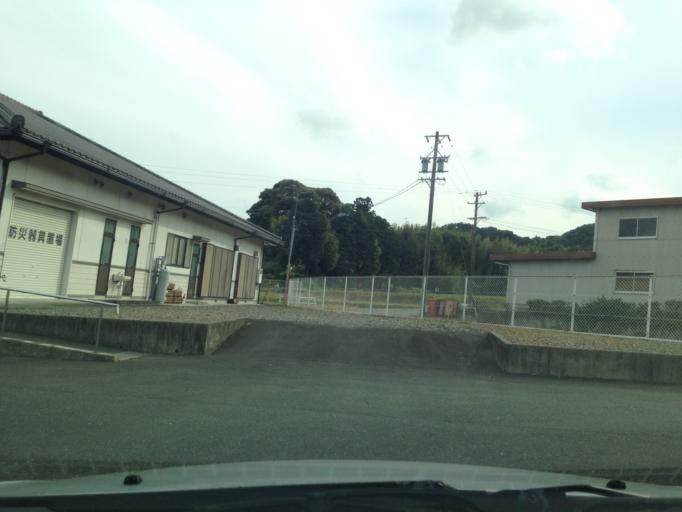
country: JP
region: Shizuoka
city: Kakegawa
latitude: 34.7201
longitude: 138.0274
